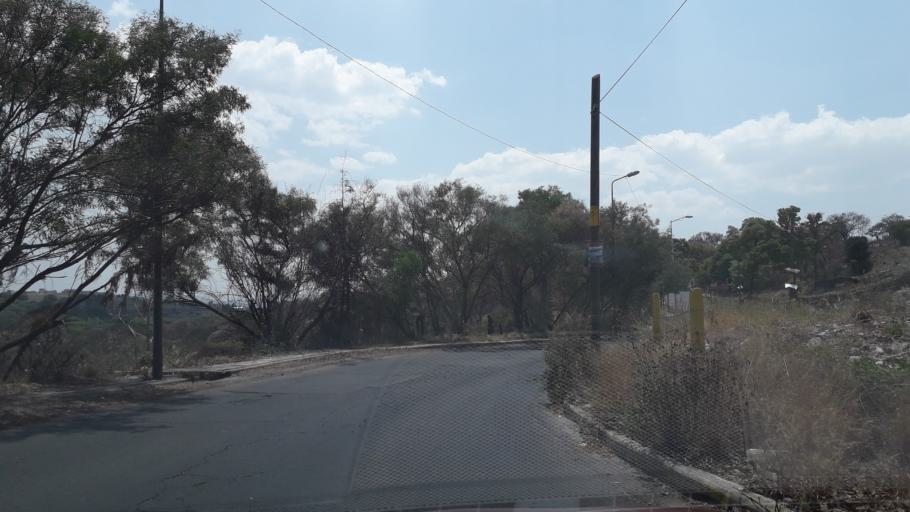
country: MX
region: Puebla
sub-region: Puebla
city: Galaxia la Calera
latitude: 18.9948
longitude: -98.1583
